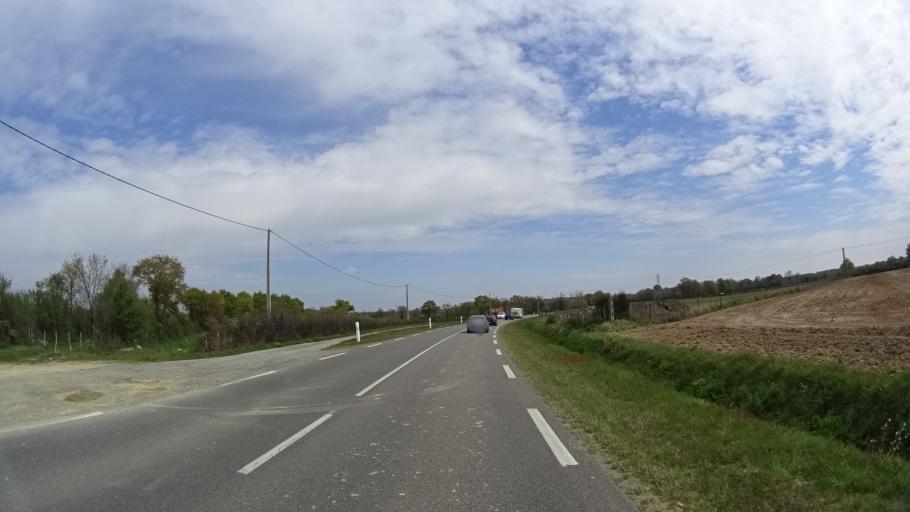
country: FR
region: Pays de la Loire
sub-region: Departement de la Loire-Atlantique
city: Saint-Hilaire-de-Chaleons
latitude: 47.0856
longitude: -1.8561
